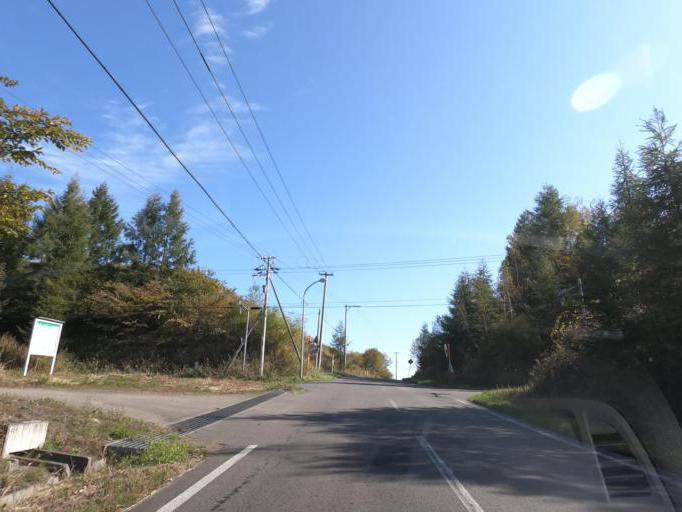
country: JP
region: Hokkaido
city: Otofuke
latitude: 42.9966
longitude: 143.2637
